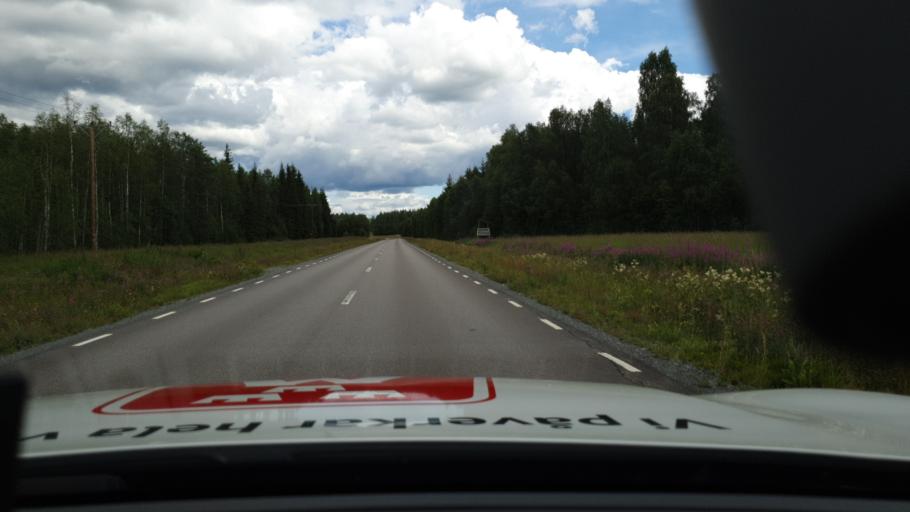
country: SE
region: Norrbotten
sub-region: Lulea Kommun
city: Sodra Sunderbyn
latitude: 65.8243
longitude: 21.9283
